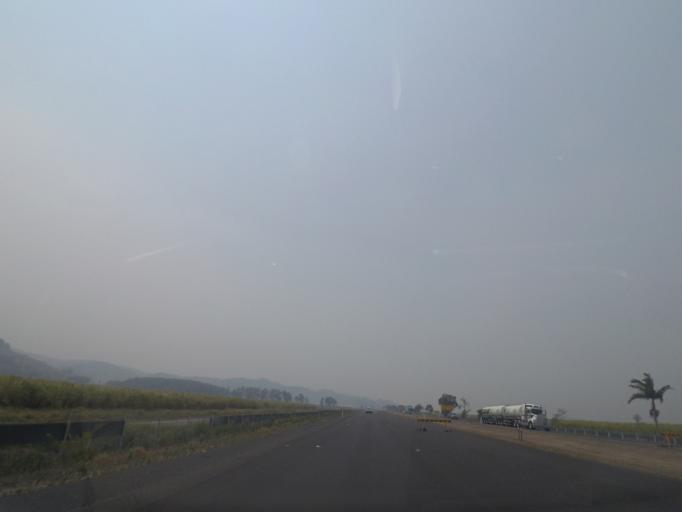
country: AU
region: New South Wales
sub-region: Ballina
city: Ballina
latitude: -28.8971
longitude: 153.4808
